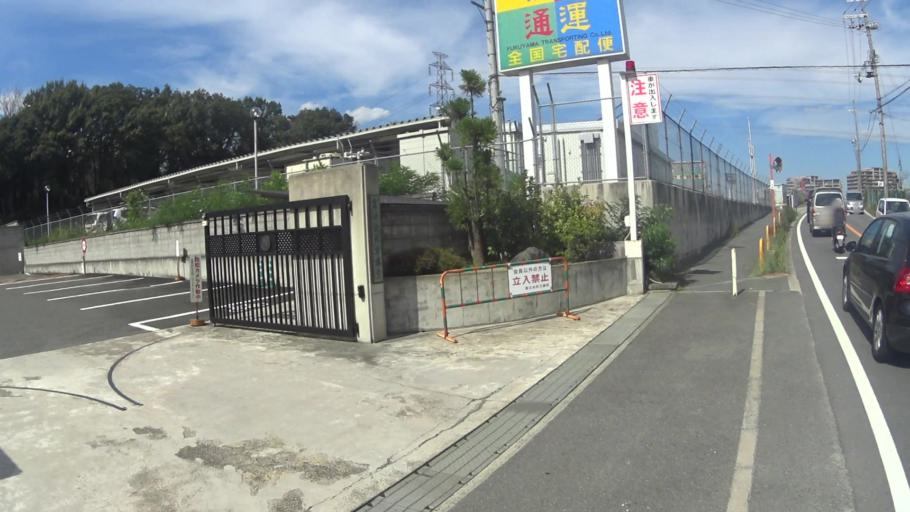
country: JP
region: Kyoto
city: Yawata
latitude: 34.8340
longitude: 135.7166
